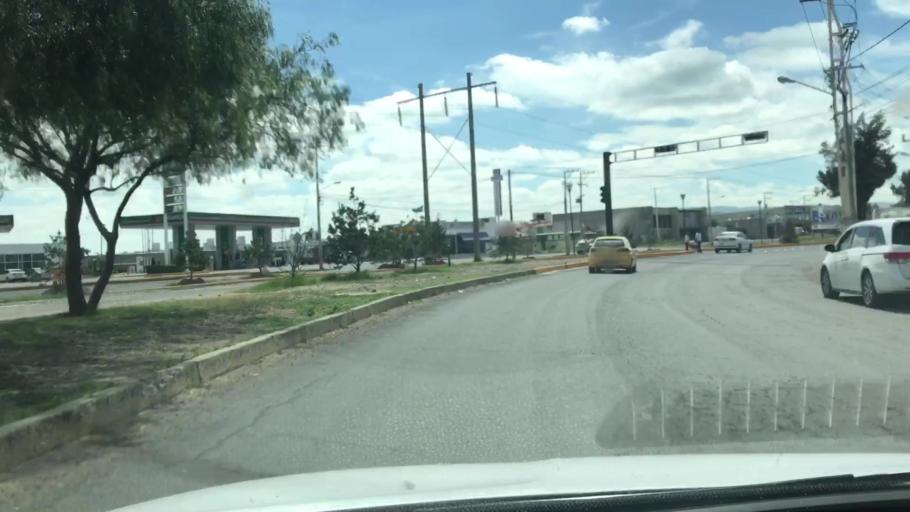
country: MX
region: Guanajuato
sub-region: Celaya
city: La Trinidad
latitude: 20.5481
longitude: -100.7815
